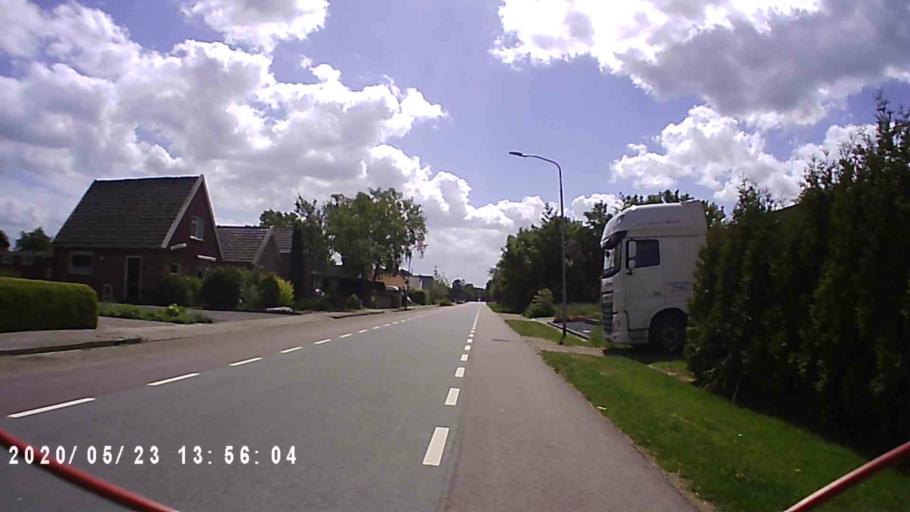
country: NL
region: Groningen
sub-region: Gemeente Delfzijl
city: Delfzijl
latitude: 53.2707
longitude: 7.0279
